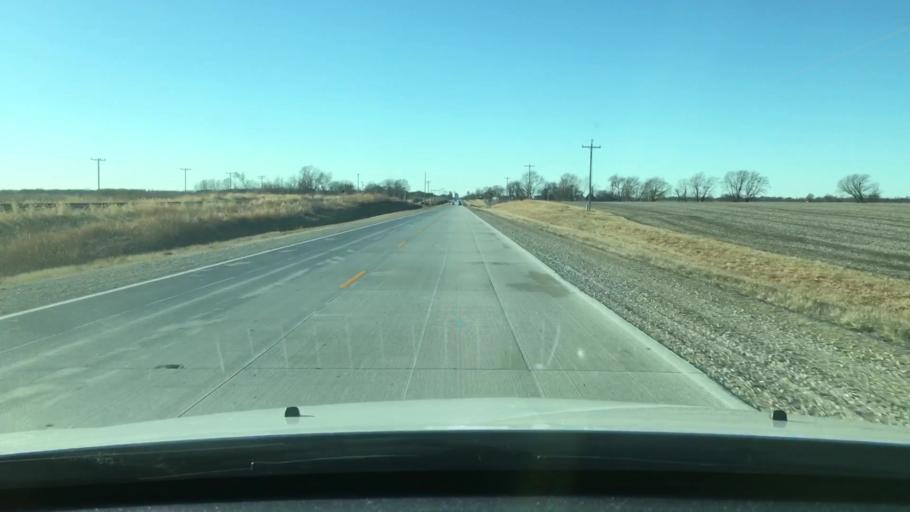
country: US
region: Missouri
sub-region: Boone County
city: Centralia
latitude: 39.2042
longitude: -92.0819
